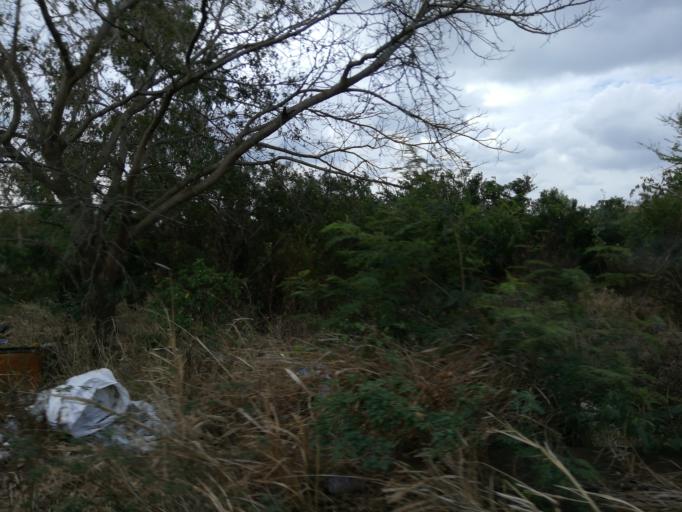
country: MU
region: Black River
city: Petite Riviere
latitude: -20.2085
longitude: 57.4606
